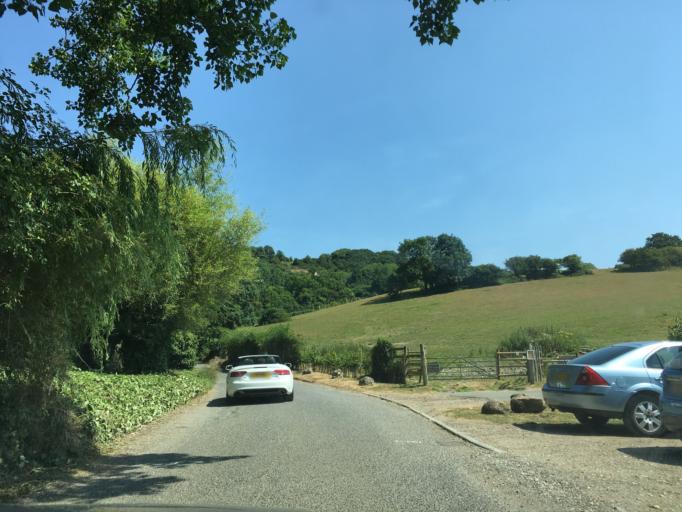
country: GB
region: England
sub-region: Isle of Wight
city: Newchurch
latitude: 50.6794
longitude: -1.2151
